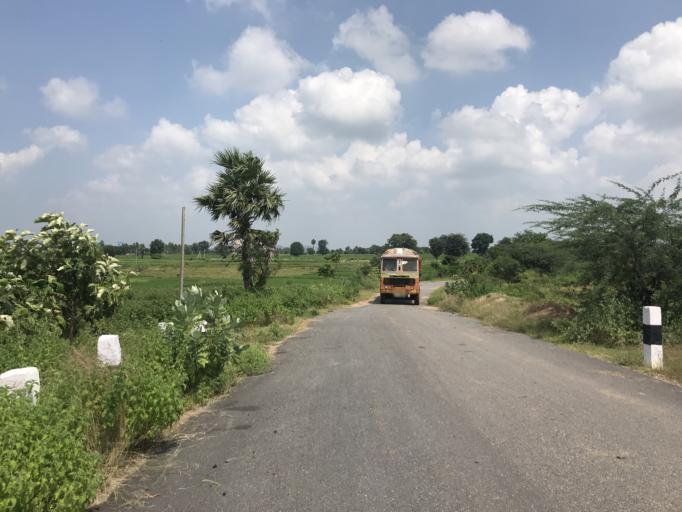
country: IN
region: Telangana
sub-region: Warangal
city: Mahbubabad
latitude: 17.6859
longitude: 79.7152
